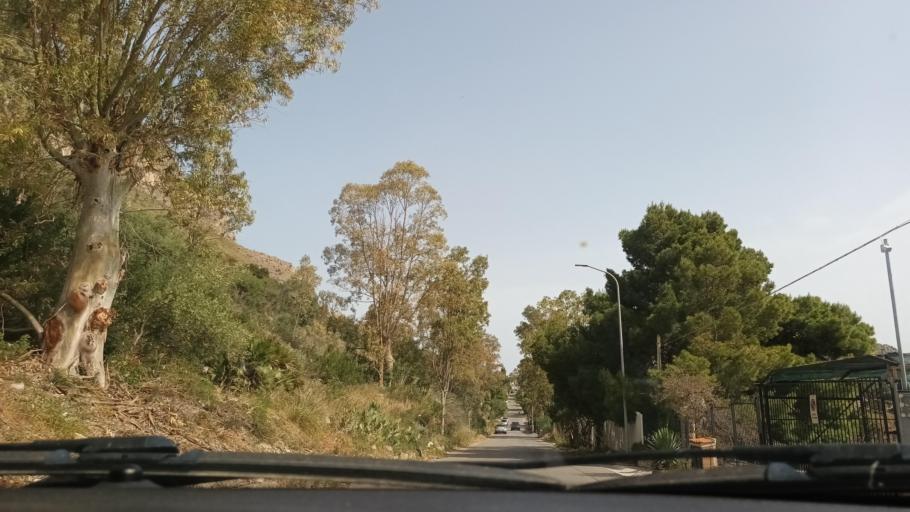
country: IT
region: Sicily
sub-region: Palermo
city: Santa Flavia
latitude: 38.0997
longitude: 13.5337
